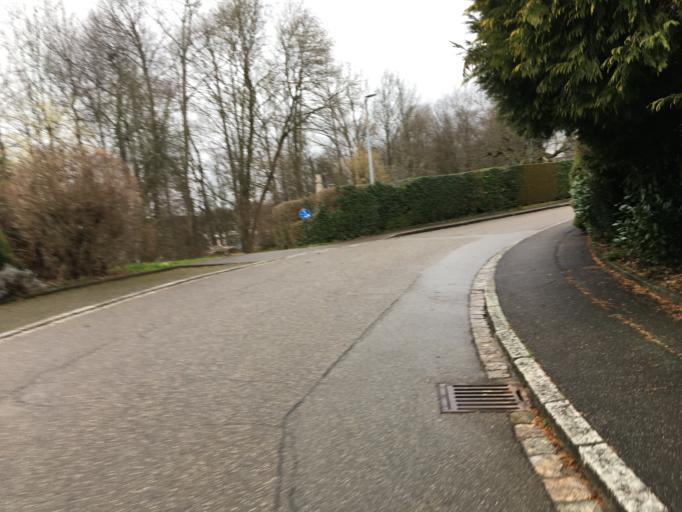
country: DE
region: Baden-Wuerttemberg
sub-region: Freiburg Region
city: Bad Sackingen
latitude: 47.5610
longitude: 7.9460
